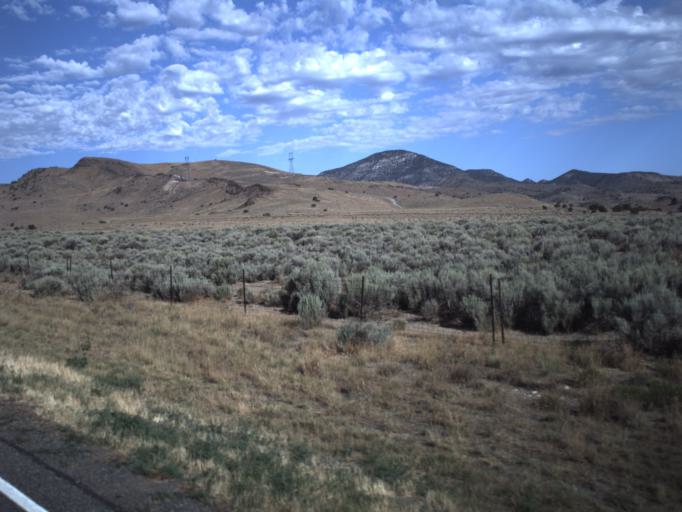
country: US
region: Utah
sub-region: Utah County
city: Genola
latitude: 39.9515
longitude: -111.9936
